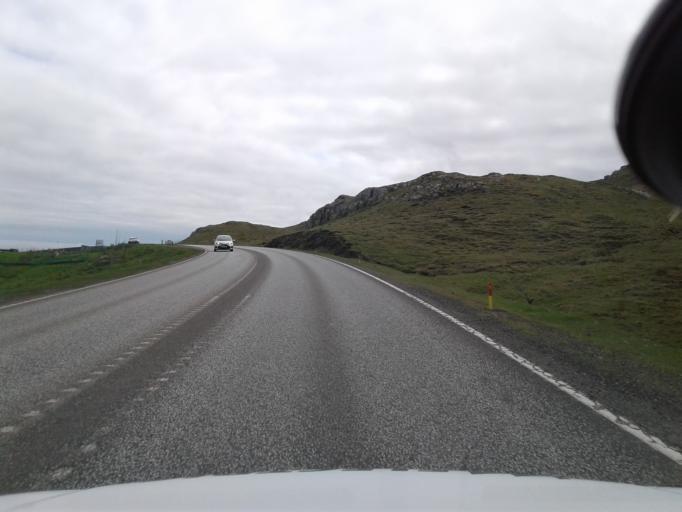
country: FO
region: Streymoy
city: Hoyvik
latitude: 62.0449
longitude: -6.7821
